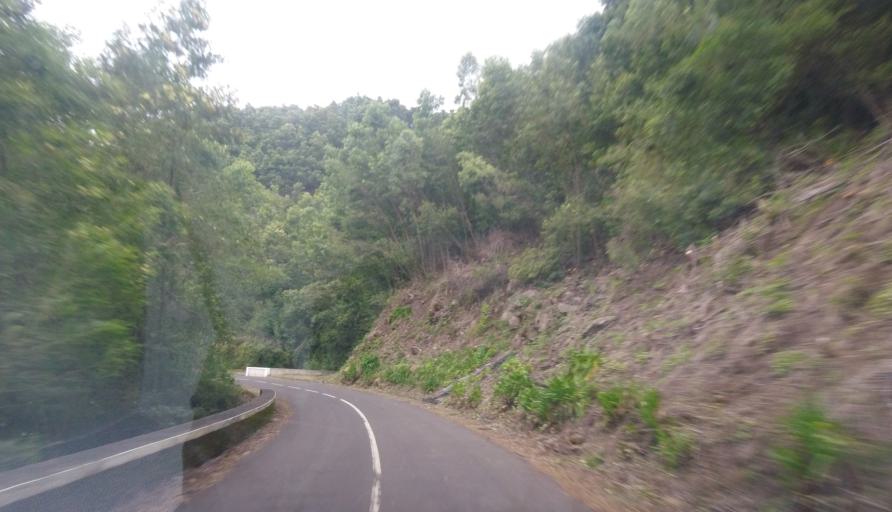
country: PT
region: Madeira
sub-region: Funchal
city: Nossa Senhora do Monte
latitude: 32.6915
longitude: -16.8927
